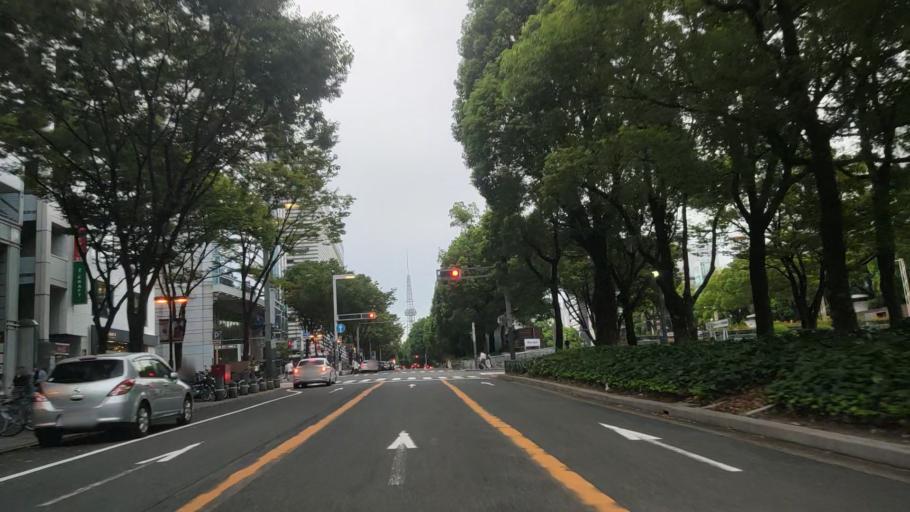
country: JP
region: Aichi
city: Nagoya-shi
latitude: 35.1637
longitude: 136.9086
